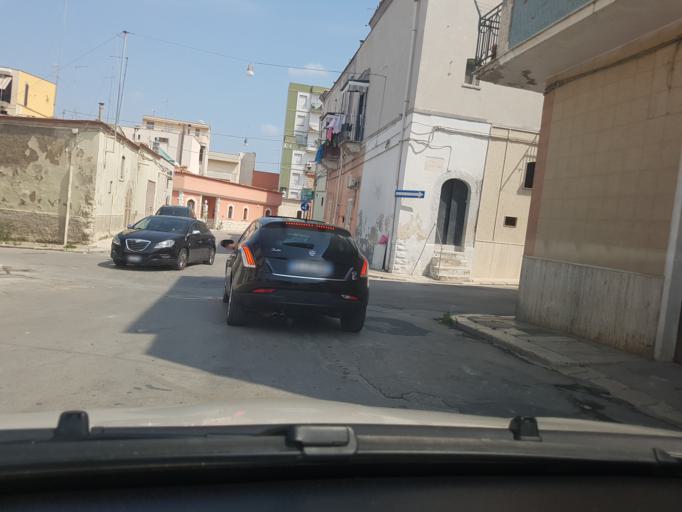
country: IT
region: Apulia
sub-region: Provincia di Foggia
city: Cerignola
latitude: 41.2678
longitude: 15.8928
